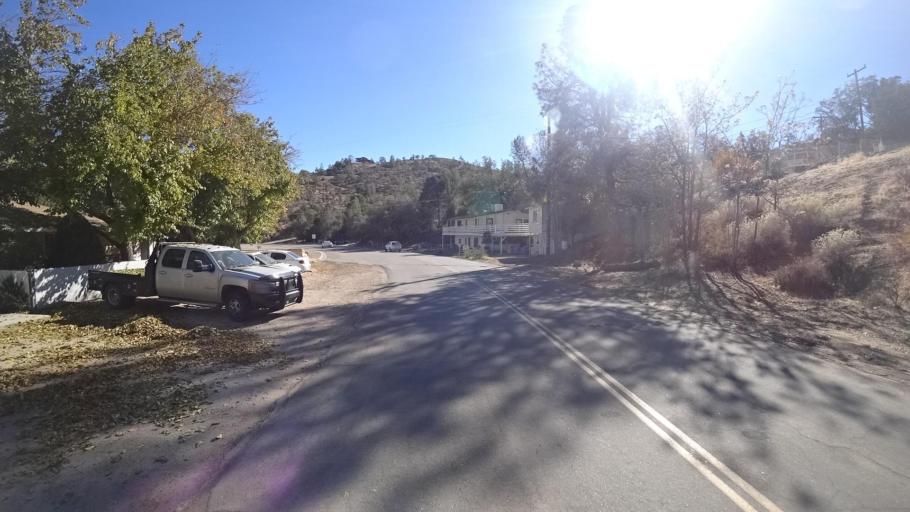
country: US
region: California
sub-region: Kern County
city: Kernville
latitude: 35.7556
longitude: -118.4285
